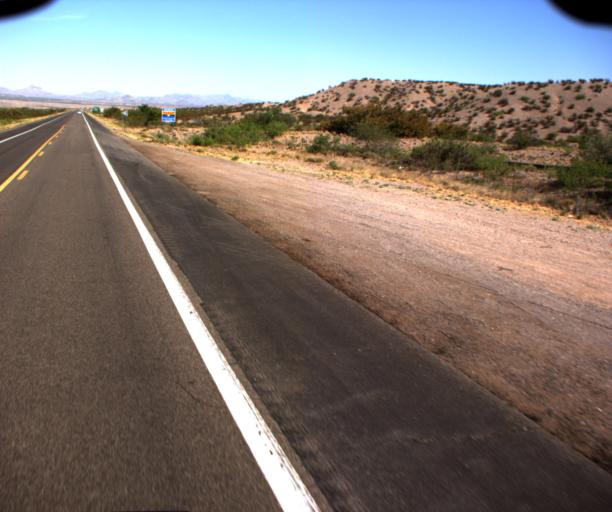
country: US
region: New Mexico
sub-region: Hidalgo County
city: Lordsburg
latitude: 32.6476
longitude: -109.0486
